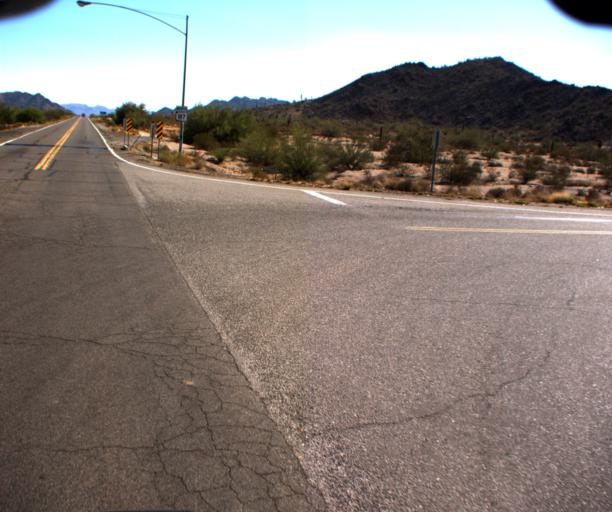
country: US
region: Arizona
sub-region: Pinal County
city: Sacaton
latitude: 33.0059
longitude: -111.7513
